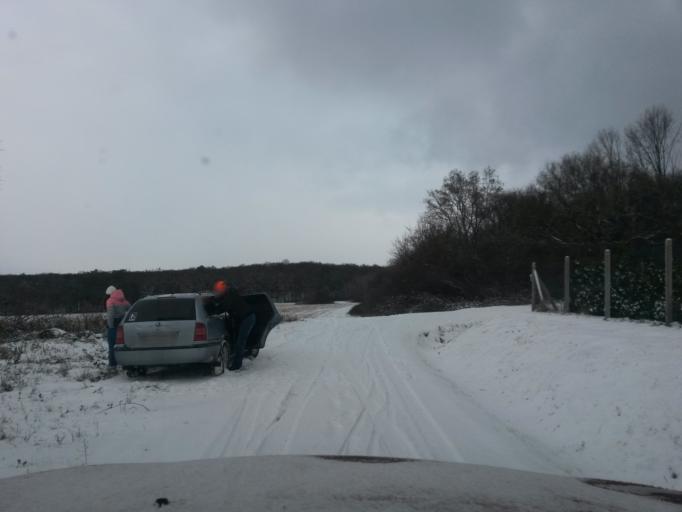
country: HU
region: Borsod-Abauj-Zemplen
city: Gonc
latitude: 48.5999
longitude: 21.3894
